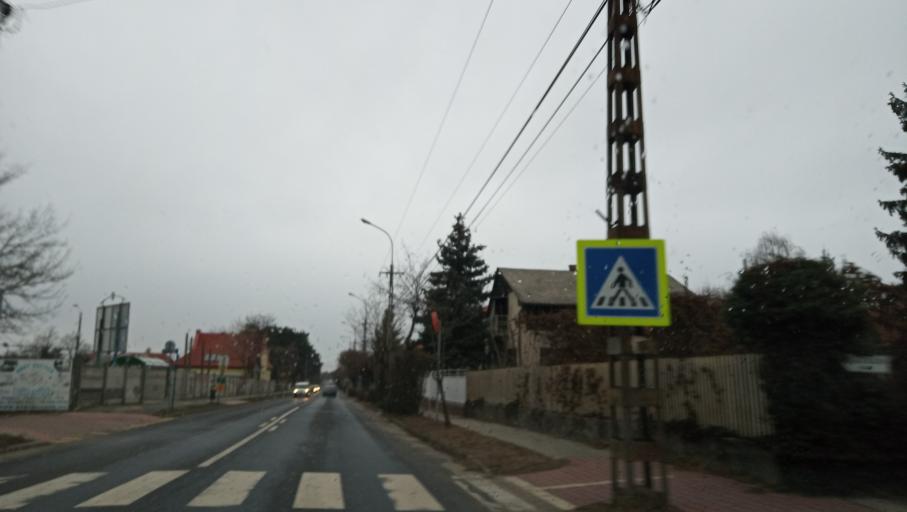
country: HU
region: Pest
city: Dunakeszi
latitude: 47.6280
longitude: 19.1466
